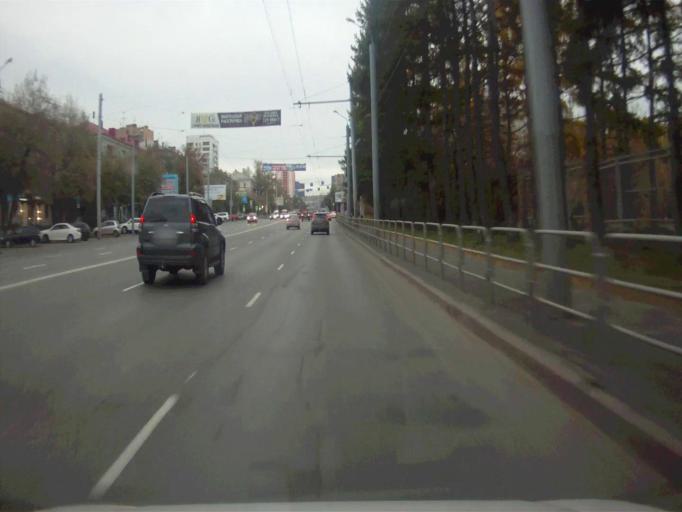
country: RU
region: Chelyabinsk
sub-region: Gorod Chelyabinsk
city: Chelyabinsk
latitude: 55.1643
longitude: 61.3807
